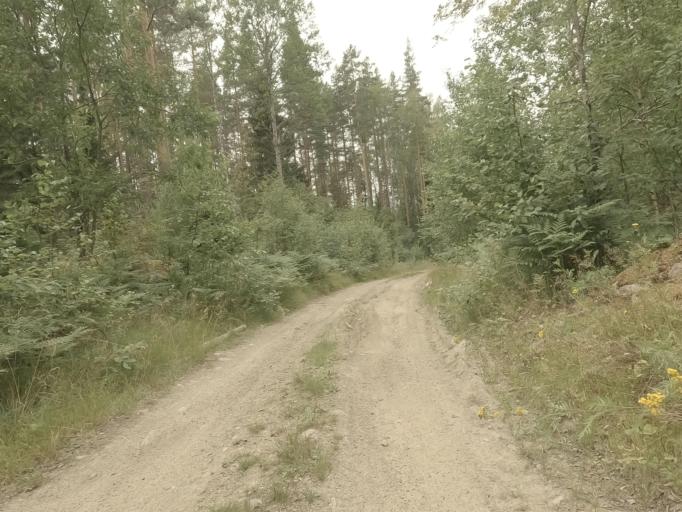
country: RU
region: Leningrad
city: Kamennogorsk
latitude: 61.0108
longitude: 29.1902
